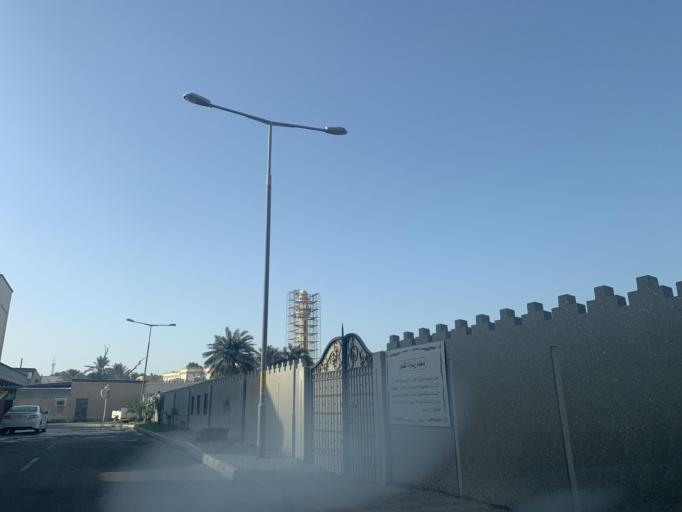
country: BH
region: Manama
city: Jidd Hafs
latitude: 26.2096
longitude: 50.4530
